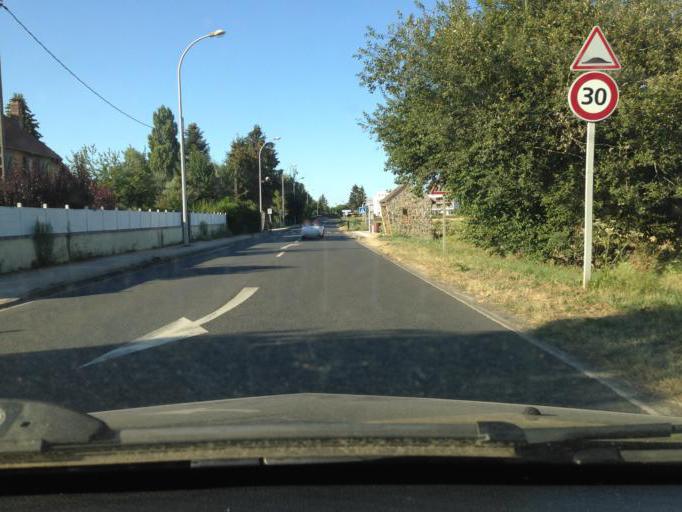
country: FR
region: Ile-de-France
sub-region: Departement des Yvelines
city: Saint-Remy-les-Chevreuse
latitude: 48.7178
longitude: 2.0869
